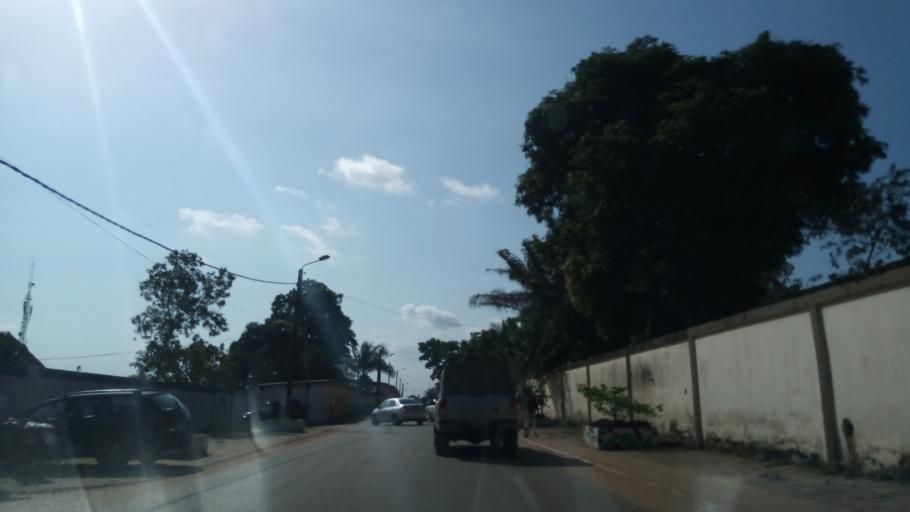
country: CI
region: Lagunes
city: Bingerville
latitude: 5.3598
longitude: -3.8882
